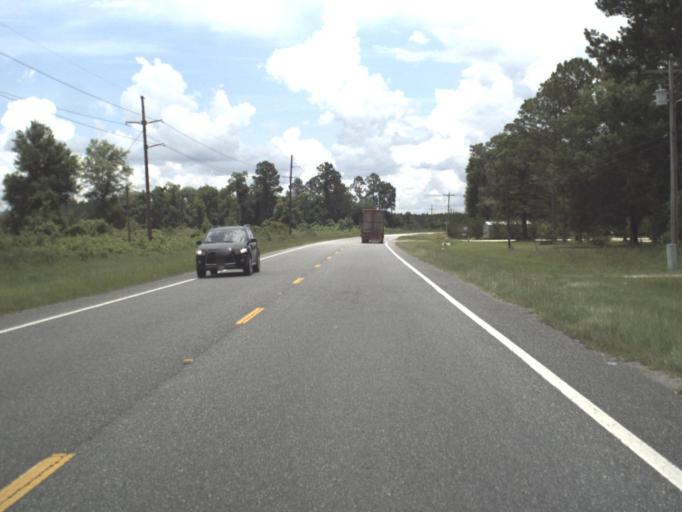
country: US
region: Florida
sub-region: Bradford County
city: Starke
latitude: 29.9578
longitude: -82.1569
